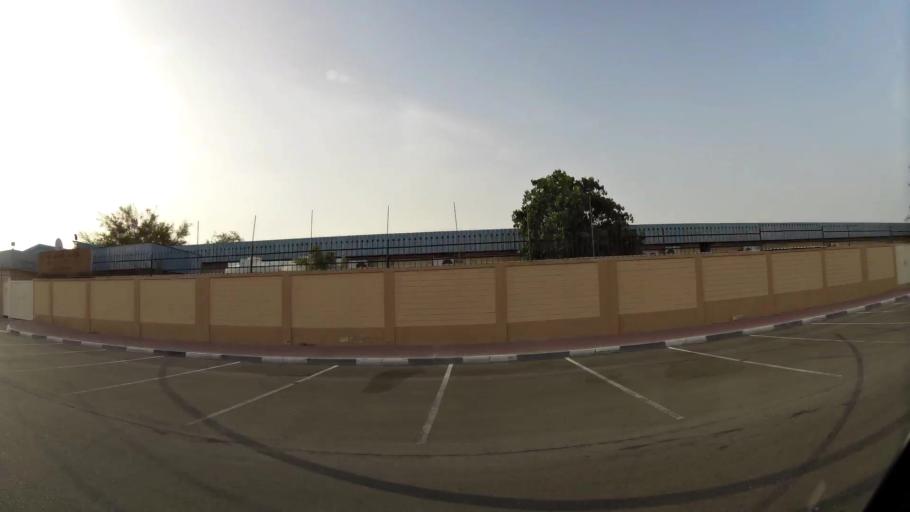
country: OM
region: Al Buraimi
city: Al Buraymi
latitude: 24.2438
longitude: 55.7455
